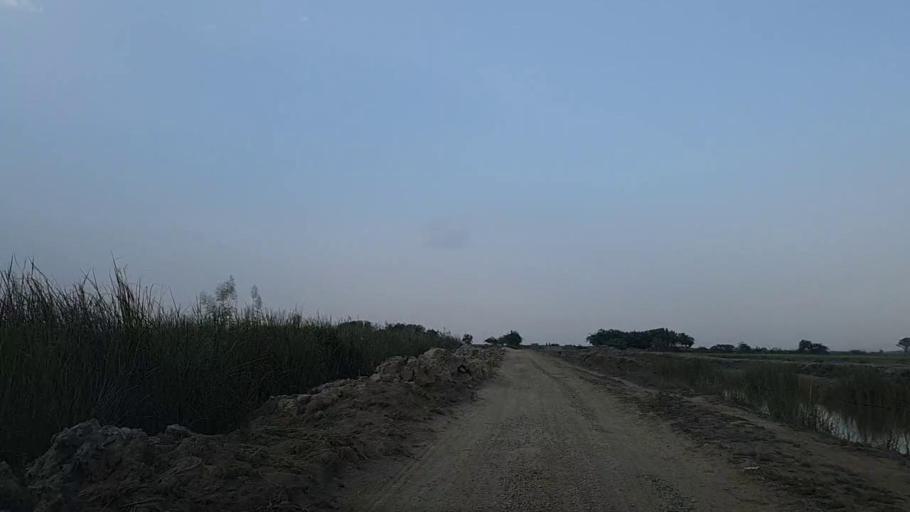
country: PK
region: Sindh
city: Daro Mehar
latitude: 24.7757
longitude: 68.1332
